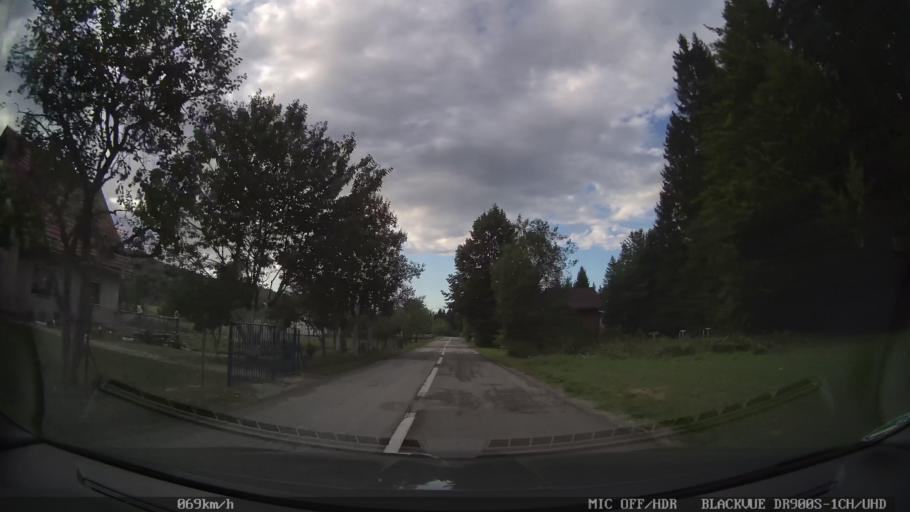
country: HR
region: Licko-Senjska
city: Jezerce
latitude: 44.9496
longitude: 15.5343
